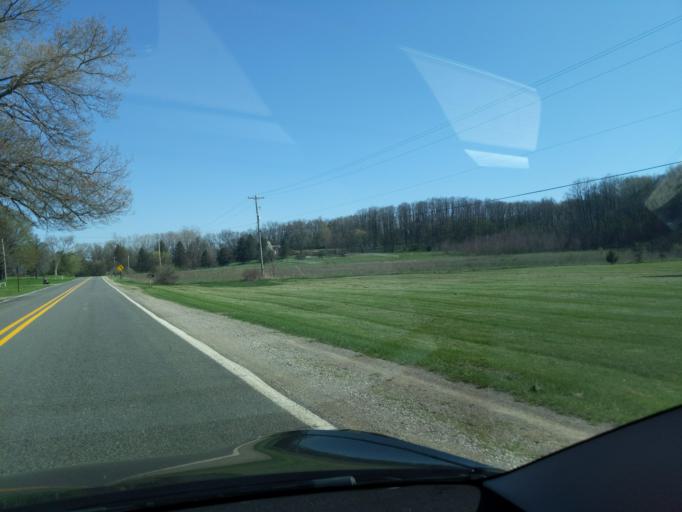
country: US
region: Michigan
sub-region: Ingham County
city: Stockbridge
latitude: 42.4351
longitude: -84.0918
